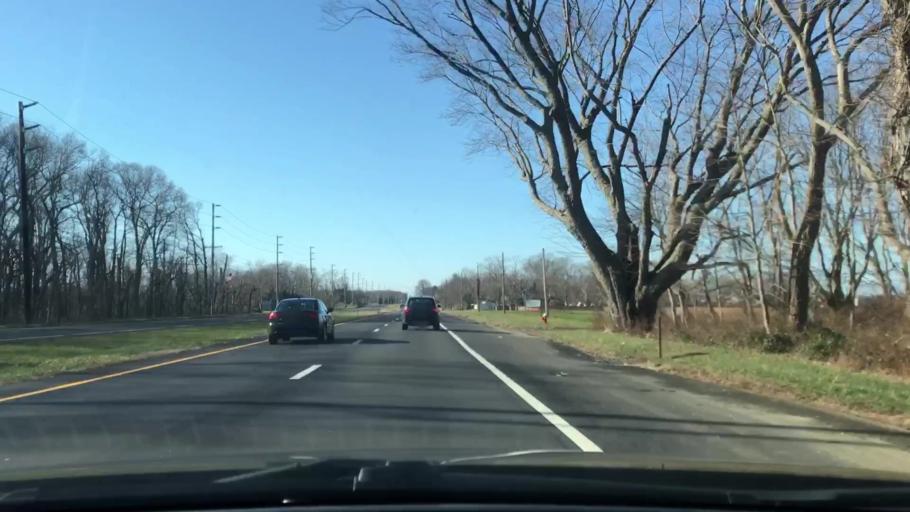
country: US
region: New York
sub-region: Suffolk County
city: Cutchogue
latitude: 41.0392
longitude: -72.4790
